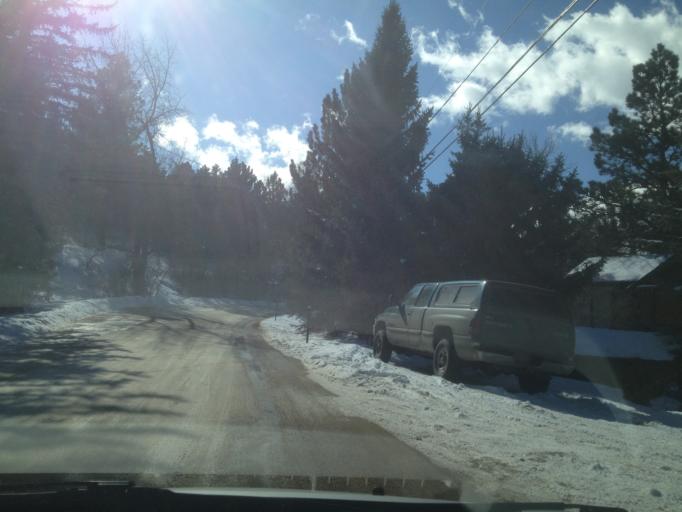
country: US
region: Colorado
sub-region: Boulder County
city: Boulder
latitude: 40.0628
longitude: -105.3134
